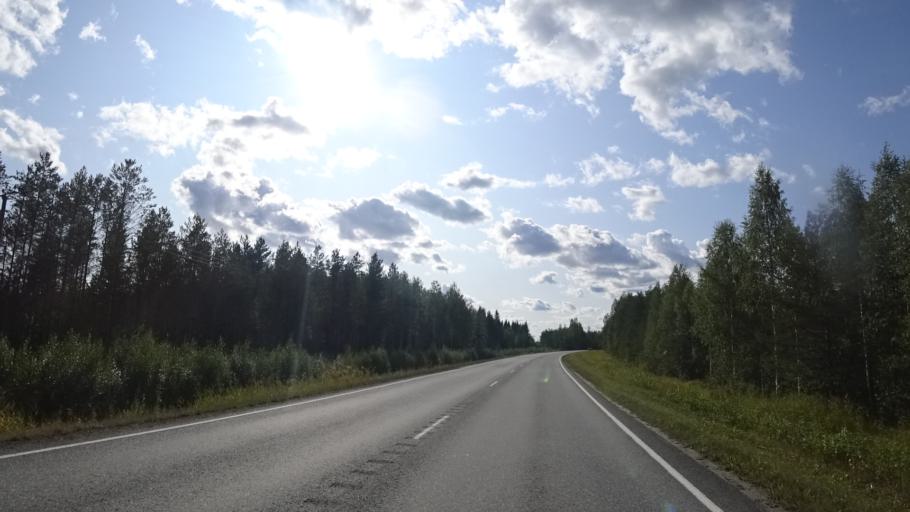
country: FI
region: North Karelia
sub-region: Keski-Karjala
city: Kitee
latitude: 62.0951
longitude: 30.0958
